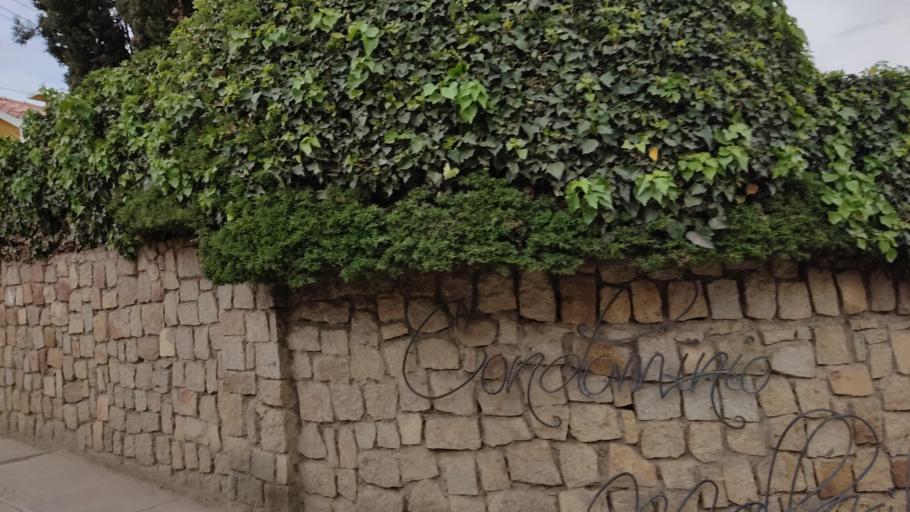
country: BO
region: La Paz
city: La Paz
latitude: -16.5653
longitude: -68.0962
